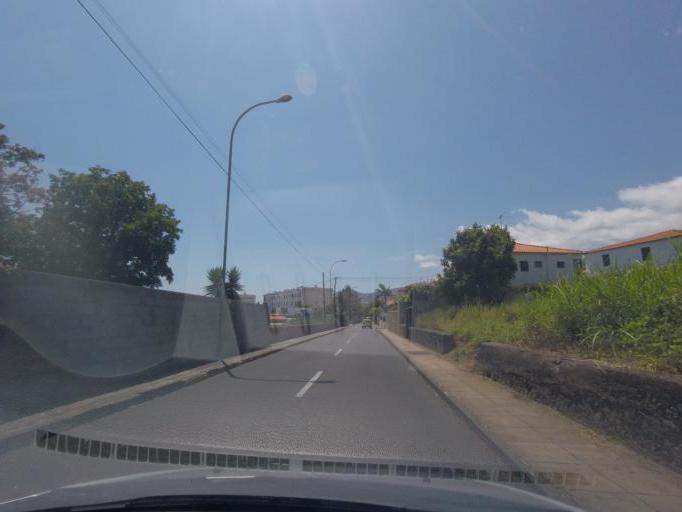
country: PT
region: Madeira
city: Camara de Lobos
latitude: 32.6592
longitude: -16.9451
